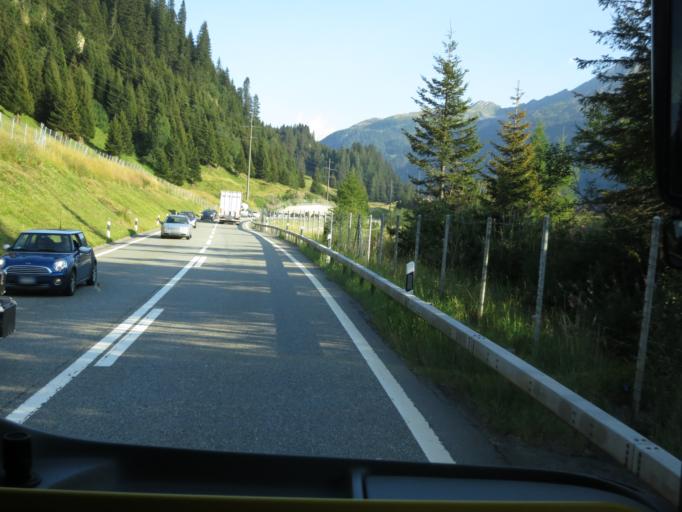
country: CH
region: Grisons
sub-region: Moesa District
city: Mesocco
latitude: 46.4496
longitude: 9.1907
